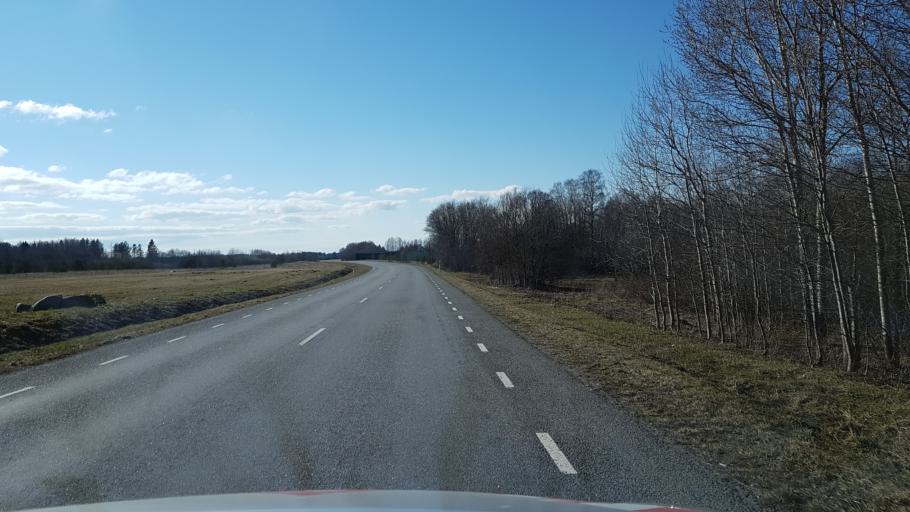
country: EE
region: Laeaene-Virumaa
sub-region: Haljala vald
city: Haljala
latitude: 59.4583
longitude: 26.2231
